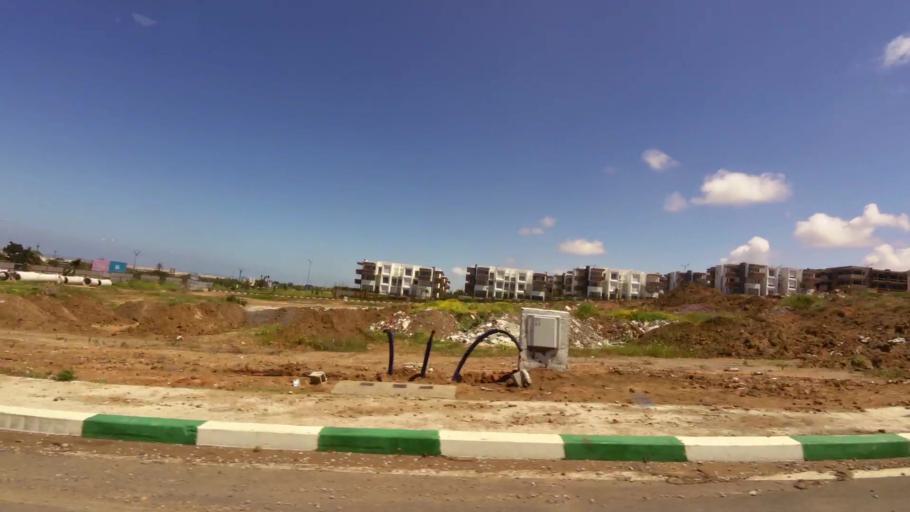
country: MA
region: Grand Casablanca
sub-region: Nouaceur
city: Dar Bouazza
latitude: 33.5252
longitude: -7.7805
